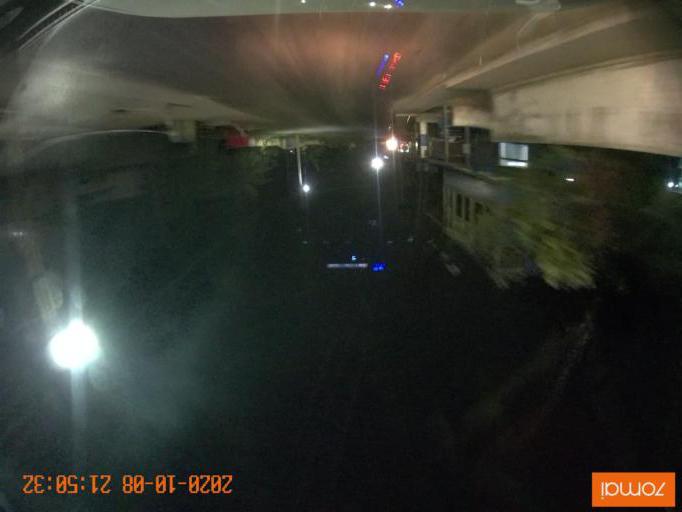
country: IN
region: Kerala
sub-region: Malappuram
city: Pariyapuram
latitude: 10.9940
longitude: 75.8731
